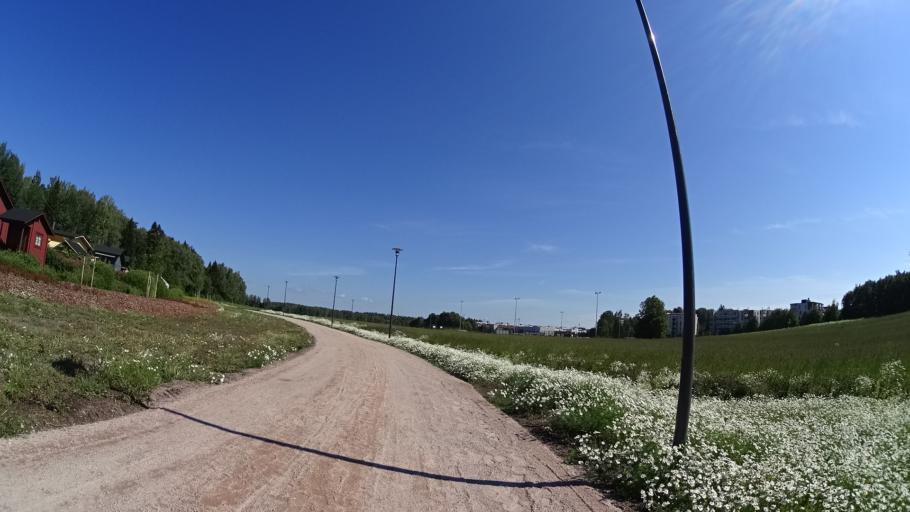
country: FI
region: Uusimaa
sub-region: Helsinki
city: Kilo
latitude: 60.2135
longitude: 24.7963
